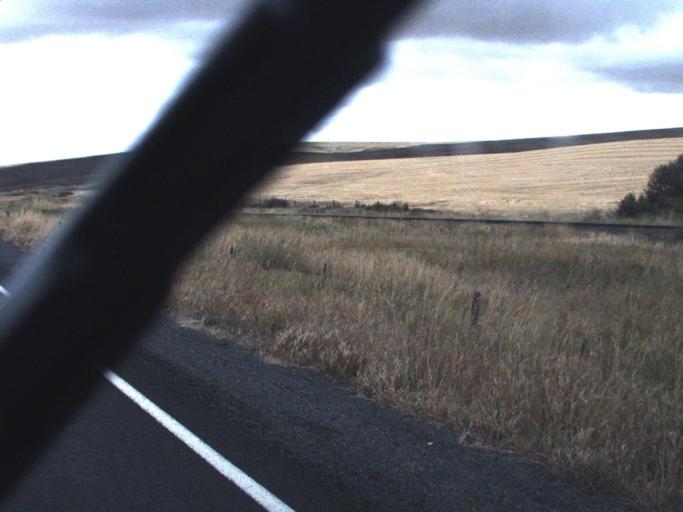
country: US
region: Washington
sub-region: Whitman County
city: Colfax
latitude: 47.1953
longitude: -117.3415
